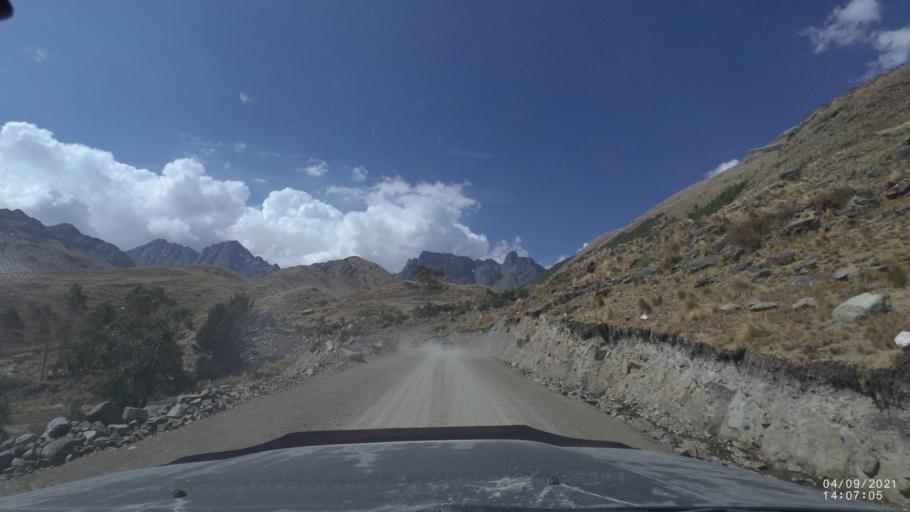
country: BO
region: Cochabamba
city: Sipe Sipe
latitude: -17.2289
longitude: -66.4681
